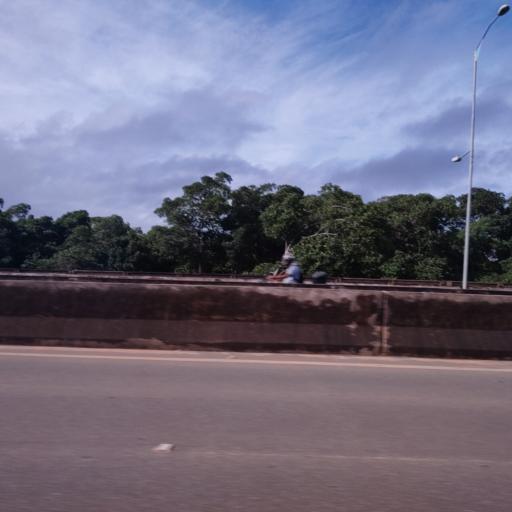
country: BR
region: Maranhao
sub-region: Sao Luis
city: Sao Luis
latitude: -2.5126
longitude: -44.2716
